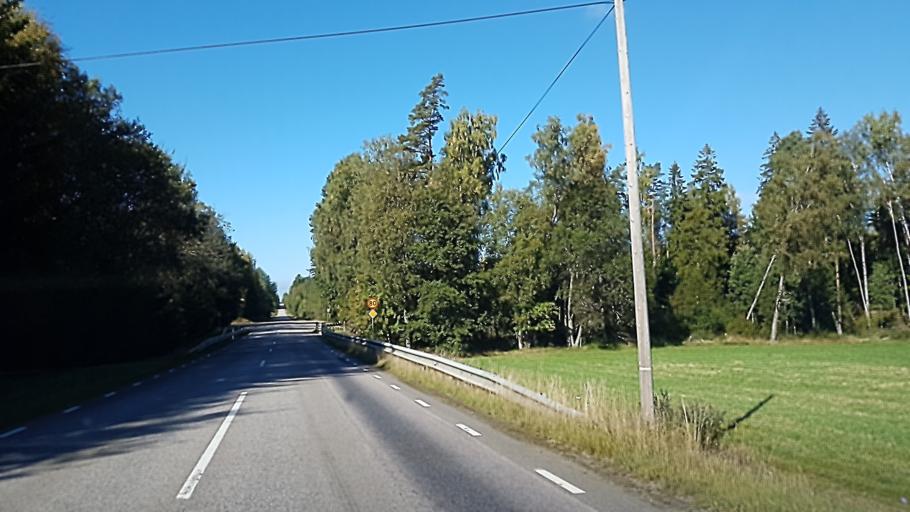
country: SE
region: Kronoberg
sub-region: Ljungby Kommun
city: Ljungby
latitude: 56.8256
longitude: 14.0535
